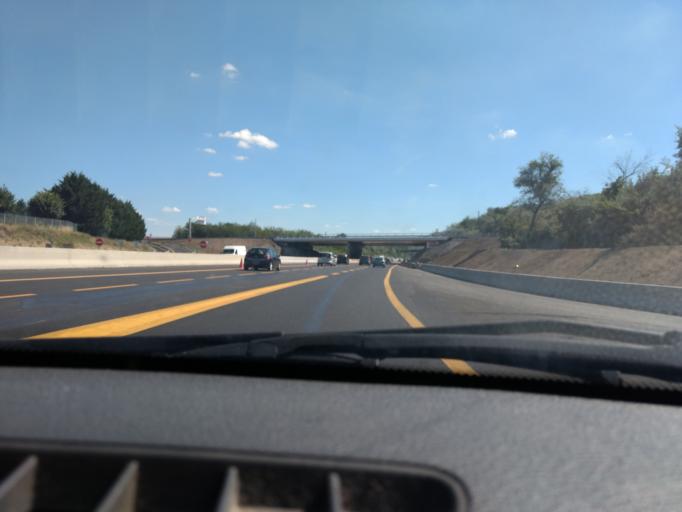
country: FR
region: Auvergne
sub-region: Departement du Puy-de-Dome
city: Aulnat
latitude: 45.7759
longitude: 3.1405
